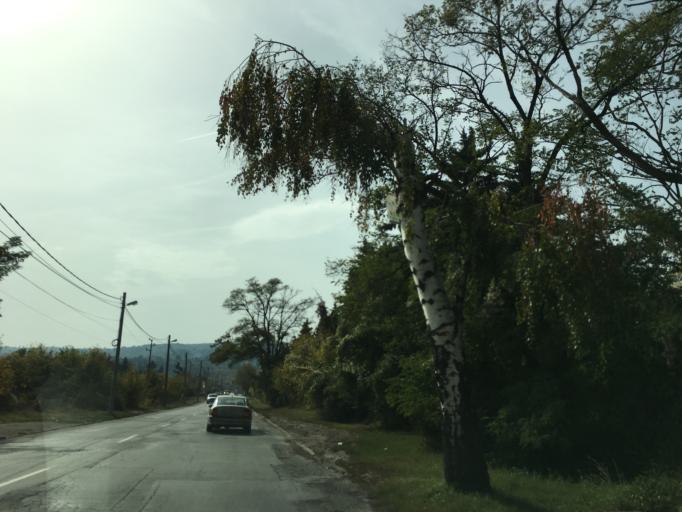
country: BG
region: Sofia-Capital
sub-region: Stolichna Obshtina
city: Sofia
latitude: 42.6186
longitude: 23.4028
